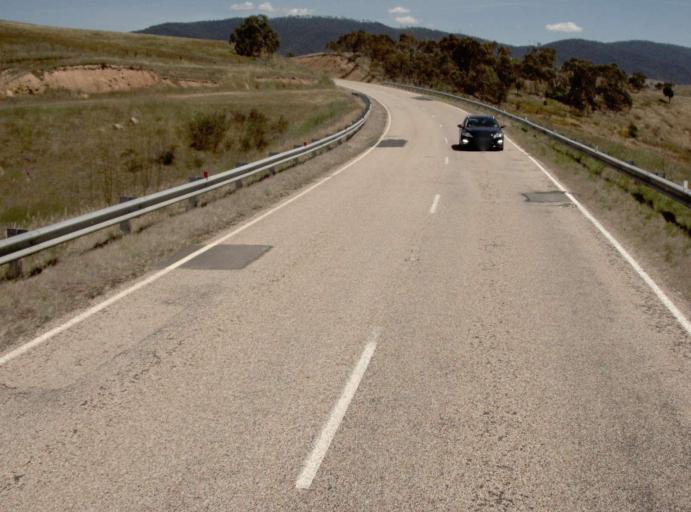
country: AU
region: Victoria
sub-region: Alpine
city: Mount Beauty
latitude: -37.1190
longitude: 147.6211
